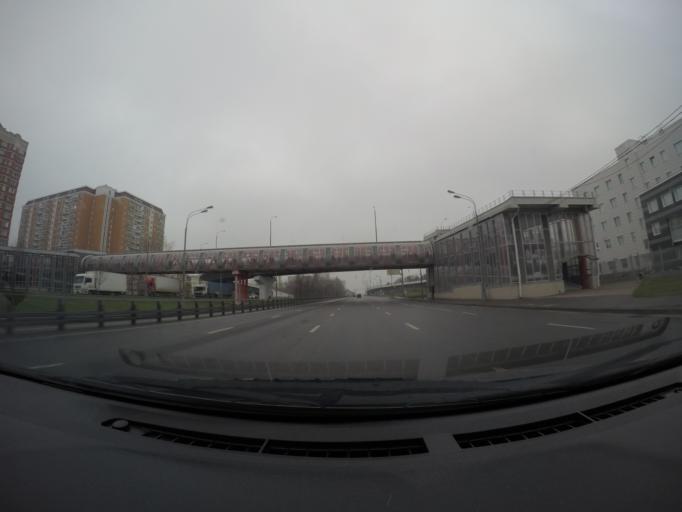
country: RU
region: Moskovskaya
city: Shcherbinka
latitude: 55.5059
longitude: 37.5738
